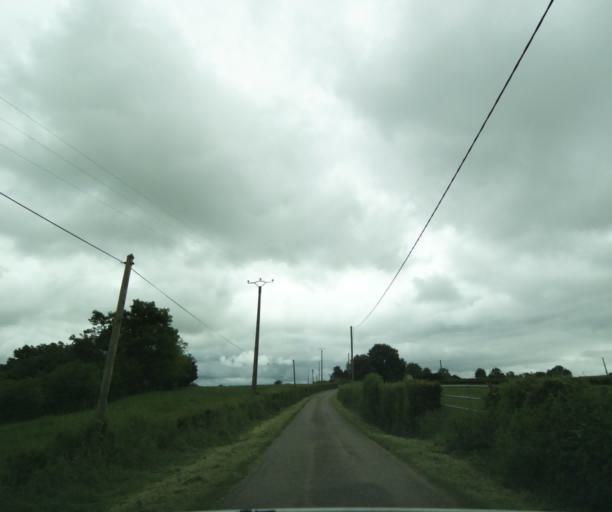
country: FR
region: Bourgogne
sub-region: Departement de Saone-et-Loire
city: Charolles
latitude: 46.4516
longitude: 4.2846
